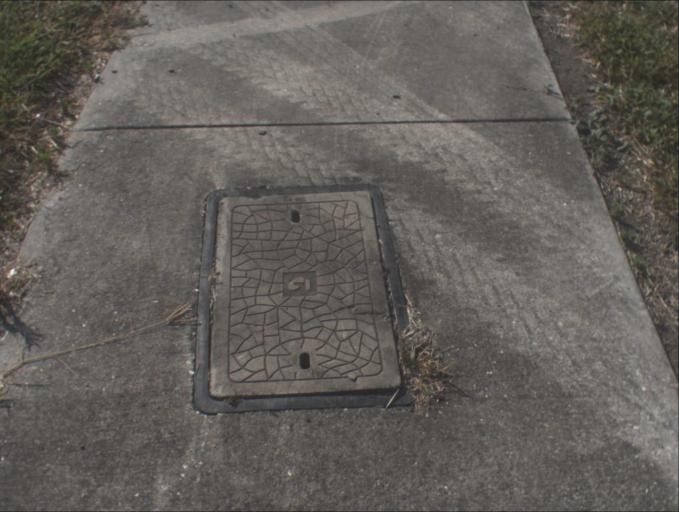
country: AU
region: Queensland
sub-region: Logan
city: Beenleigh
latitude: -27.7182
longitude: 153.1806
